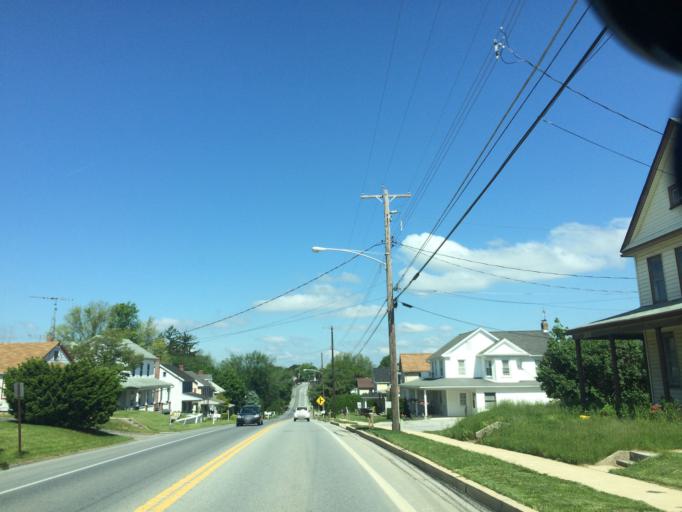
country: US
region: Pennsylvania
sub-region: York County
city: Parkville
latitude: 39.7389
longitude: -76.9370
